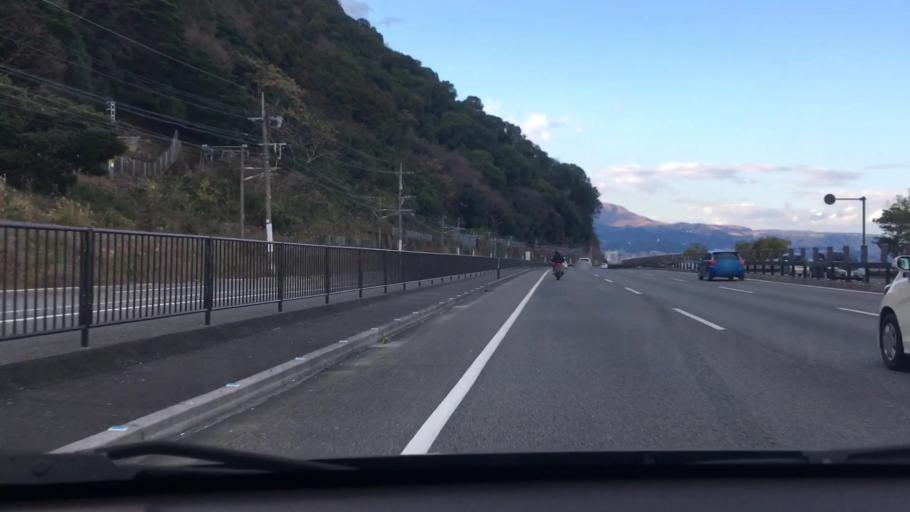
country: JP
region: Oita
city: Beppu
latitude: 33.2604
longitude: 131.5316
